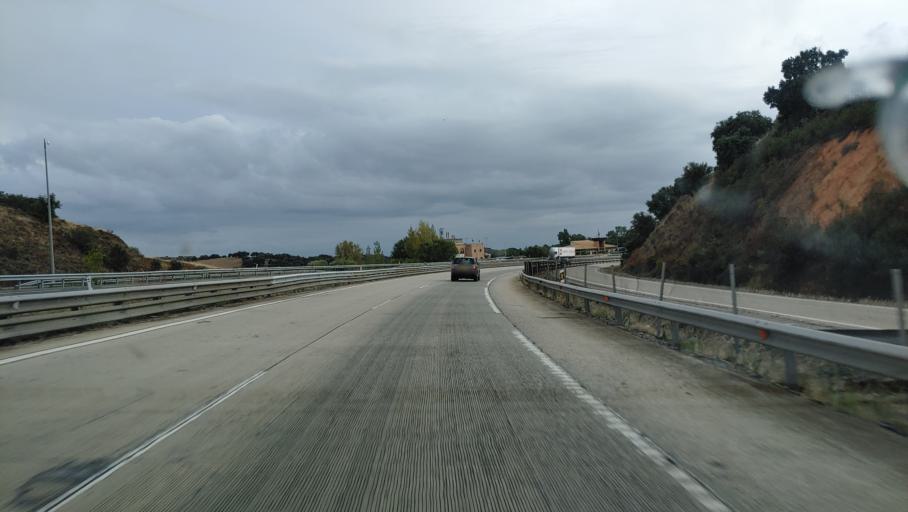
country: ES
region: Andalusia
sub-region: Provincia de Jaen
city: Santa Elena
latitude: 38.3326
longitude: -3.5420
